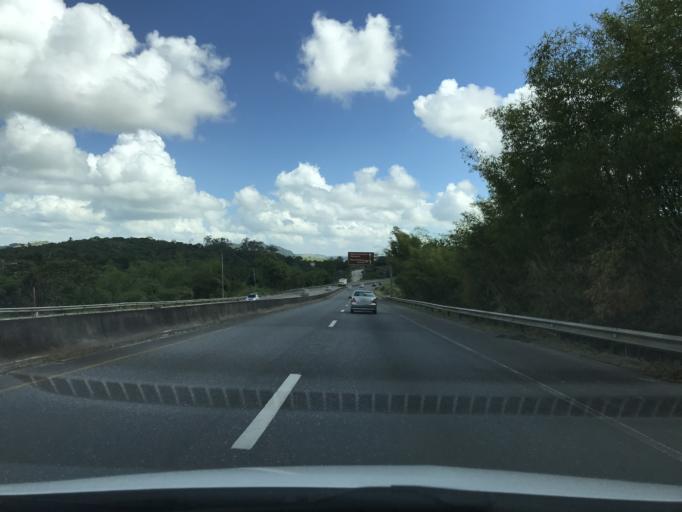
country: BR
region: Pernambuco
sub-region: Moreno
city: Moreno
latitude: -8.1126
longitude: -35.1100
